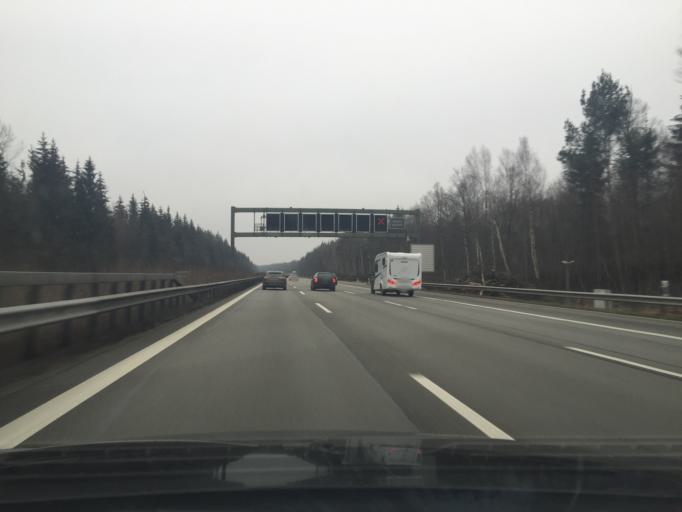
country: DE
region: Bavaria
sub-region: Upper Bavaria
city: Otterfing
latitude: 47.9205
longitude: 11.7128
